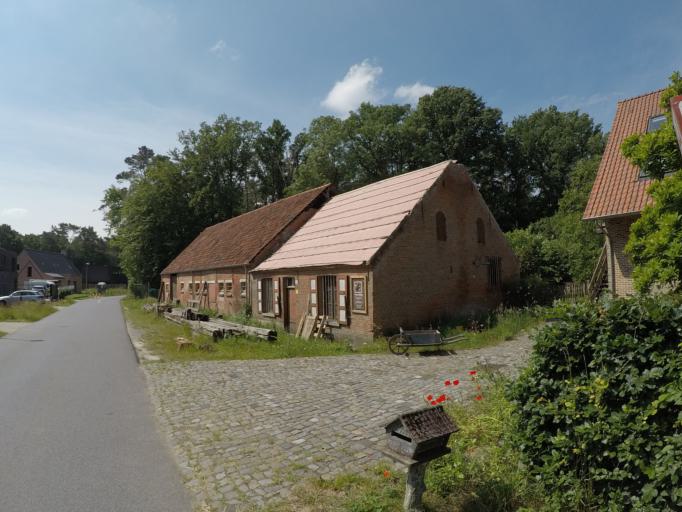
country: BE
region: Flanders
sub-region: Provincie Antwerpen
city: Zandhoven
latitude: 51.2404
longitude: 4.6300
